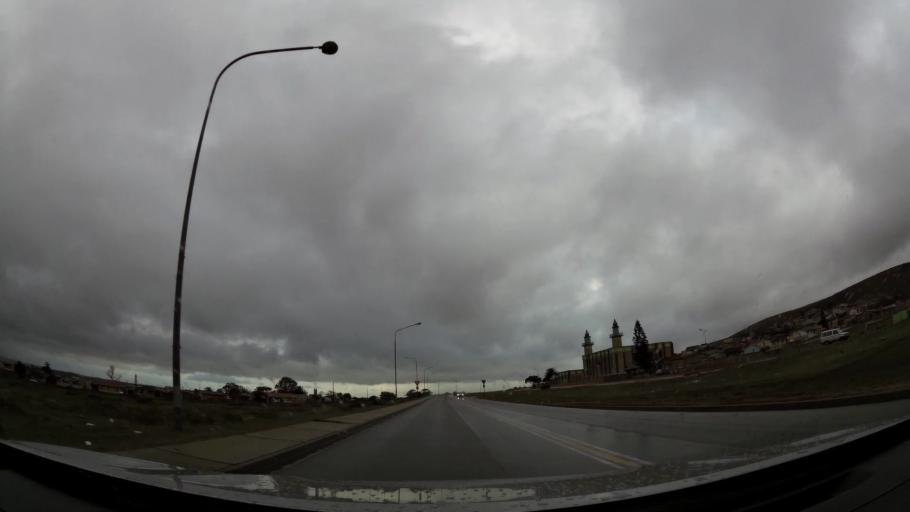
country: ZA
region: Eastern Cape
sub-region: Nelson Mandela Bay Metropolitan Municipality
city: Port Elizabeth
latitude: -33.8877
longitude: 25.5166
